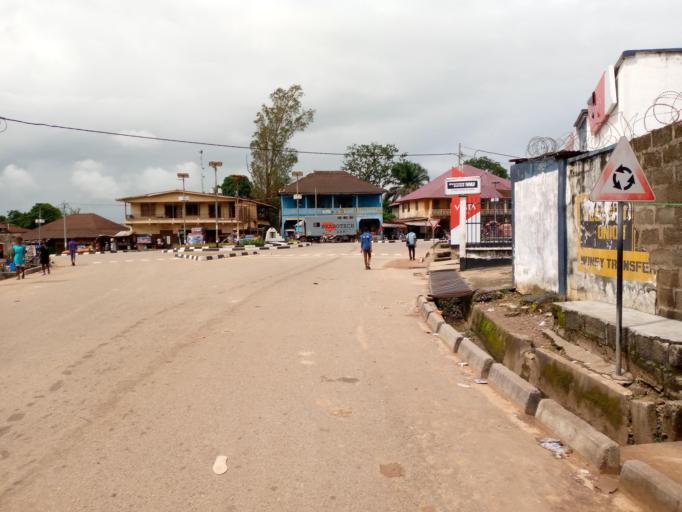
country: SL
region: Northern Province
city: Magburaka
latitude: 8.7239
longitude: -11.9492
